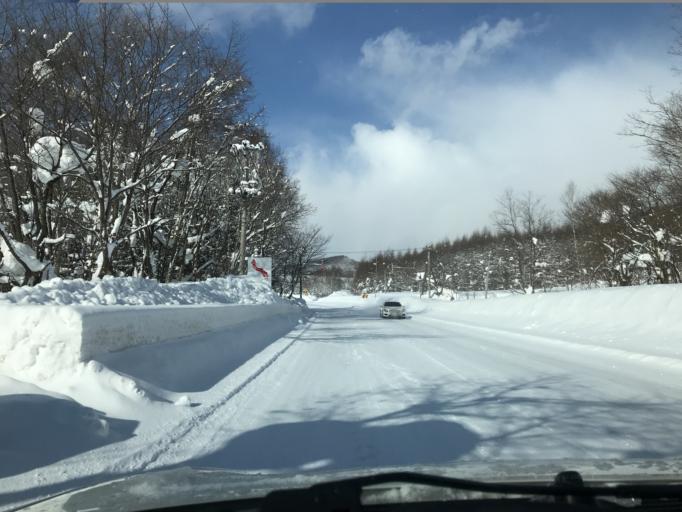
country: JP
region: Hokkaido
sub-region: Asahikawa-shi
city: Asahikawa
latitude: 43.9317
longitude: 142.4718
